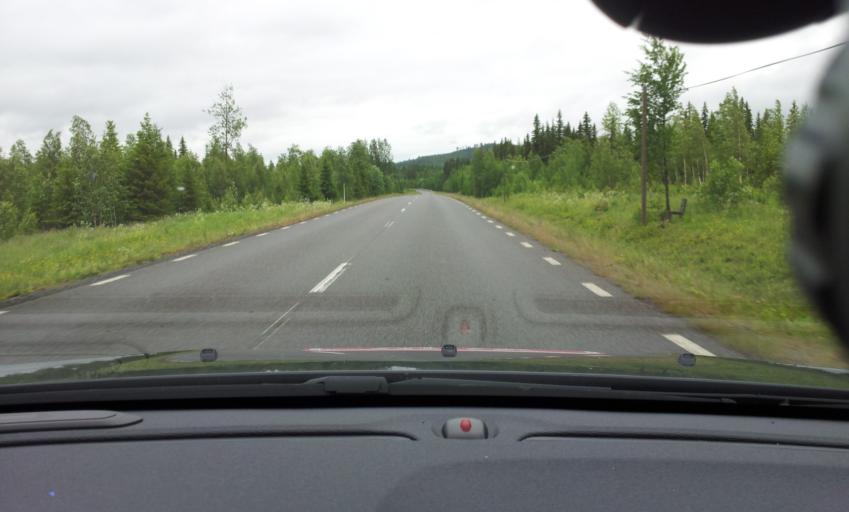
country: SE
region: Jaemtland
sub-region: OEstersunds Kommun
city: Lit
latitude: 63.6897
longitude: 15.0133
